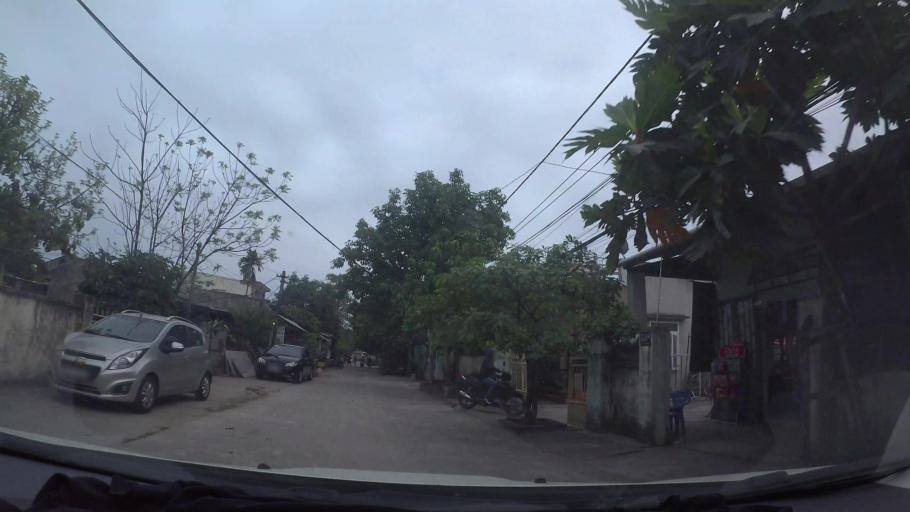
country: VN
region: Da Nang
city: Lien Chieu
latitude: 16.0866
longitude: 108.1537
